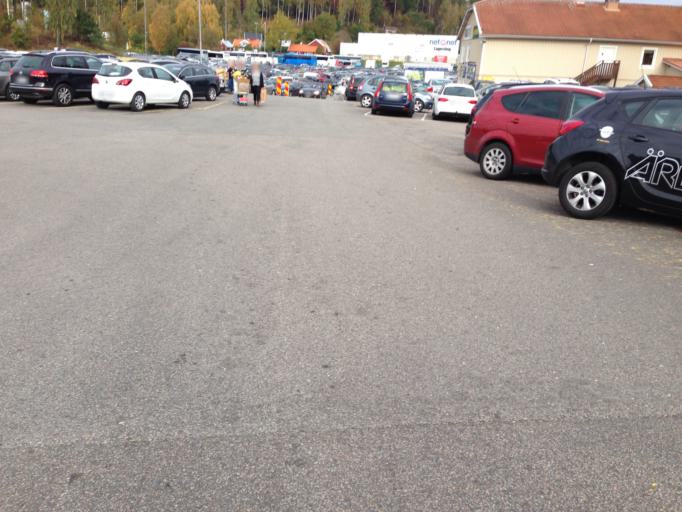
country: SE
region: Halland
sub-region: Falkenbergs Kommun
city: Falkenberg
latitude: 57.1347
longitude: 12.7114
